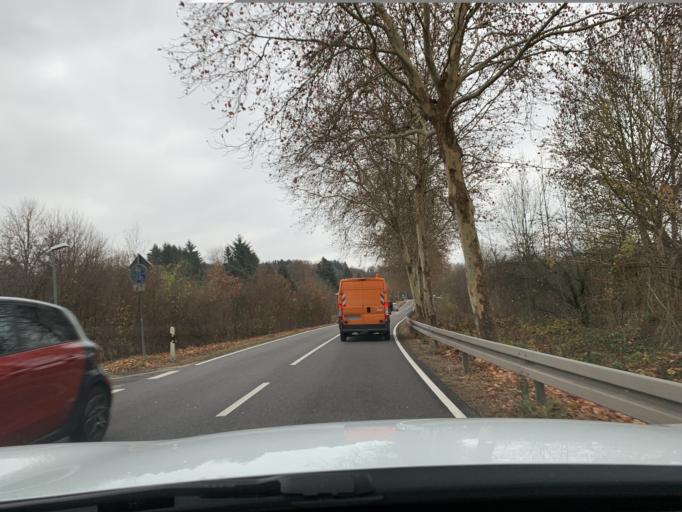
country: DE
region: Saarland
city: Kleinblittersdorf
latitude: 49.1464
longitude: 7.0451
